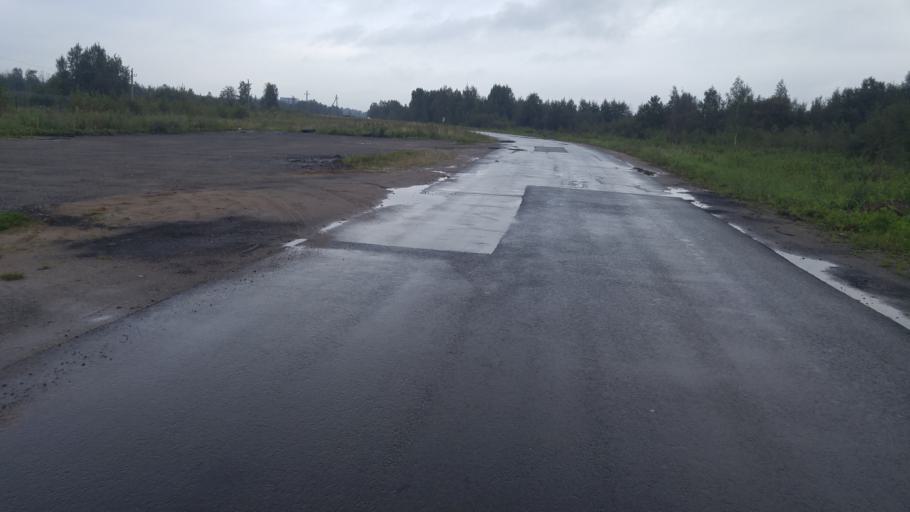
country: RU
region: St.-Petersburg
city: Metallostroy
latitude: 59.7808
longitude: 30.5695
